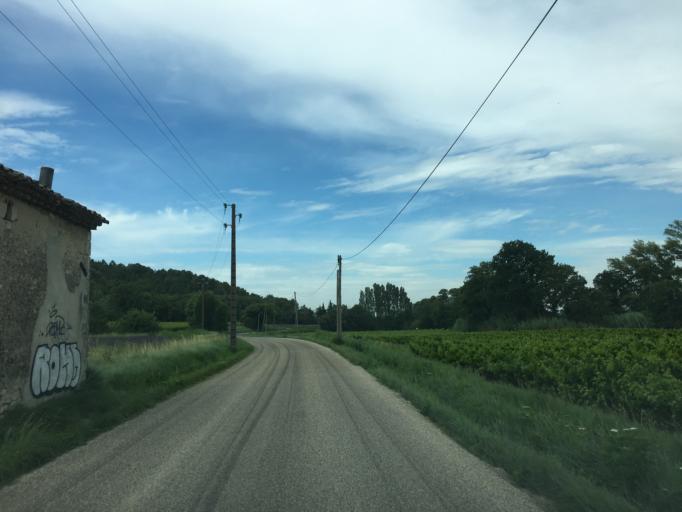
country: FR
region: Provence-Alpes-Cote d'Azur
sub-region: Departement du Vaucluse
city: Bollene
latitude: 44.3031
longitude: 4.7747
